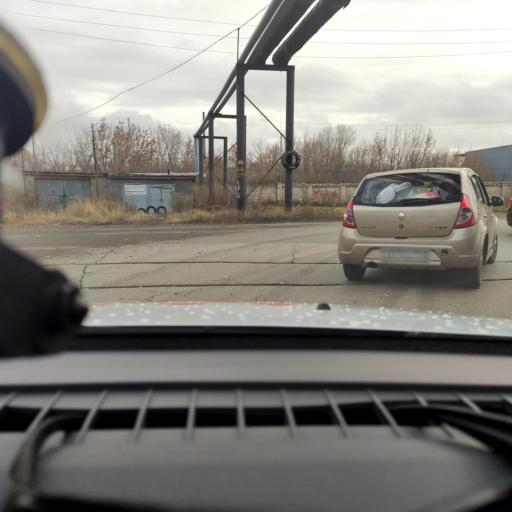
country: RU
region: Samara
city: Chapayevsk
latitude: 52.9826
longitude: 49.7226
